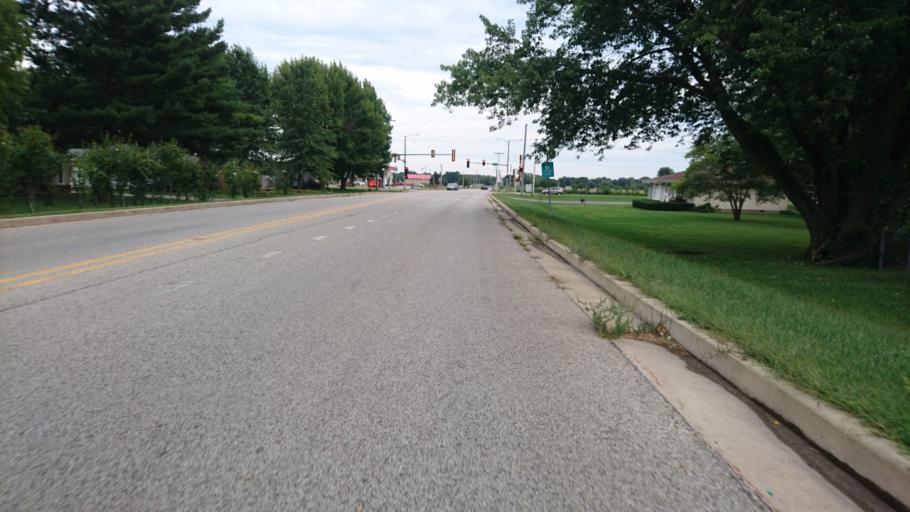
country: US
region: Illinois
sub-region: Sangamon County
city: Chatham
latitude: 39.6766
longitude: -89.6970
